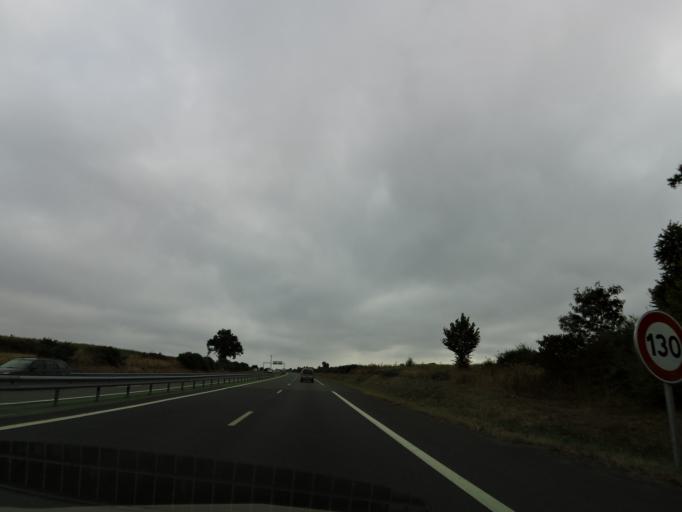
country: FR
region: Pays de la Loire
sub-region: Departement de la Vendee
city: La Ferriere
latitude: 46.6741
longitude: -1.3426
